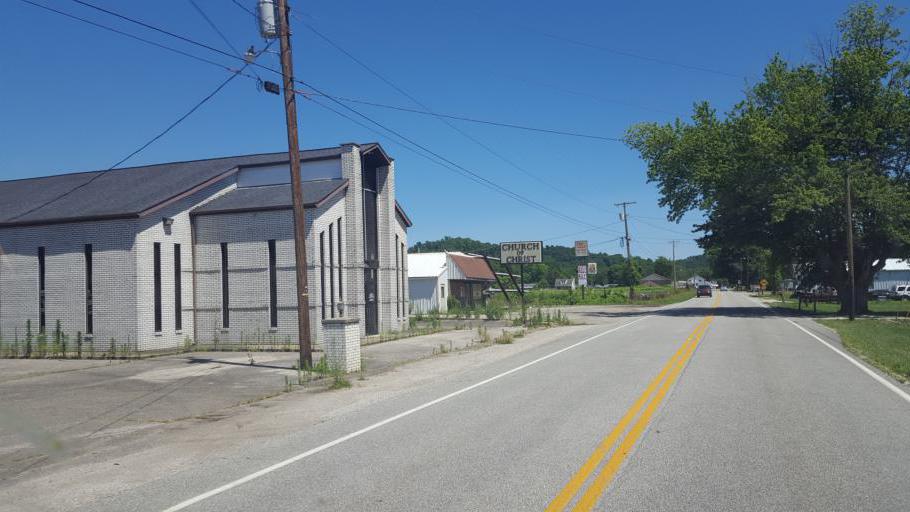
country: US
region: West Virginia
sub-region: Cabell County
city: Lesage
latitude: 38.5339
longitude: -82.3026
